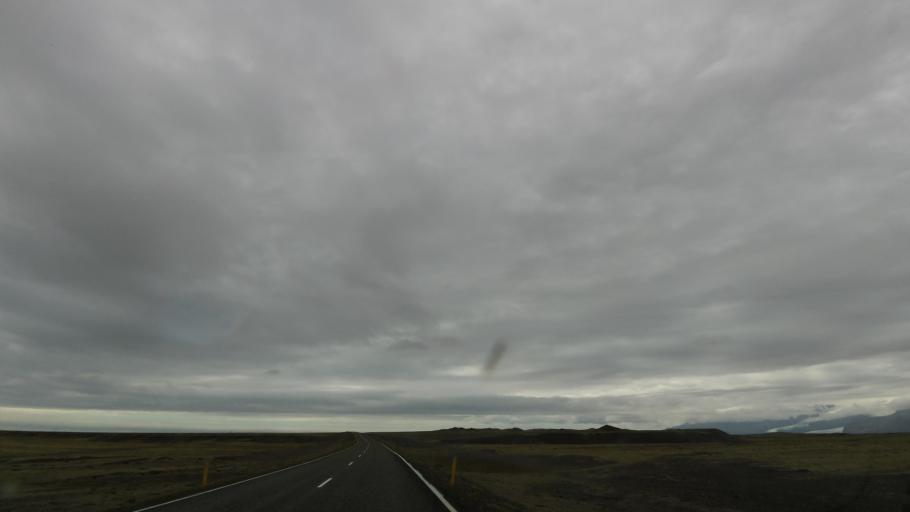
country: IS
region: East
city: Hoefn
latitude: 64.1070
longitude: -16.0957
